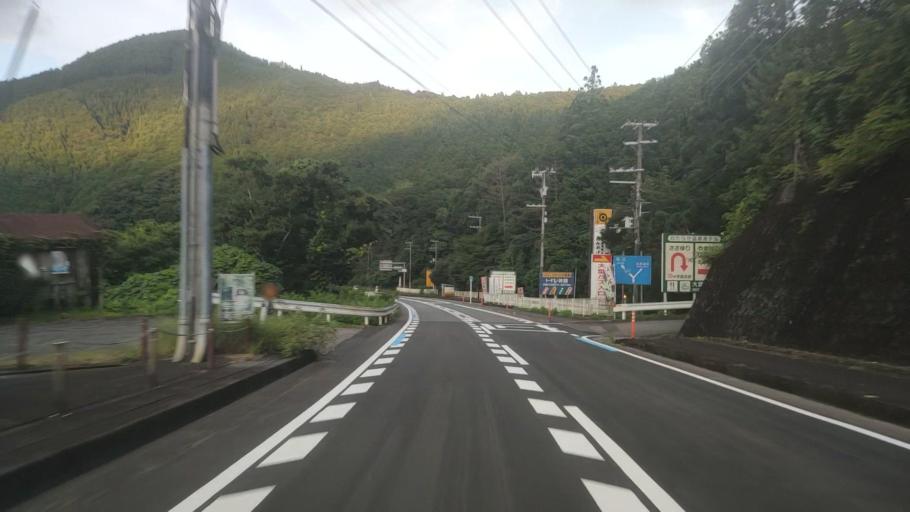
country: JP
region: Wakayama
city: Shingu
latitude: 33.8176
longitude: 135.7632
